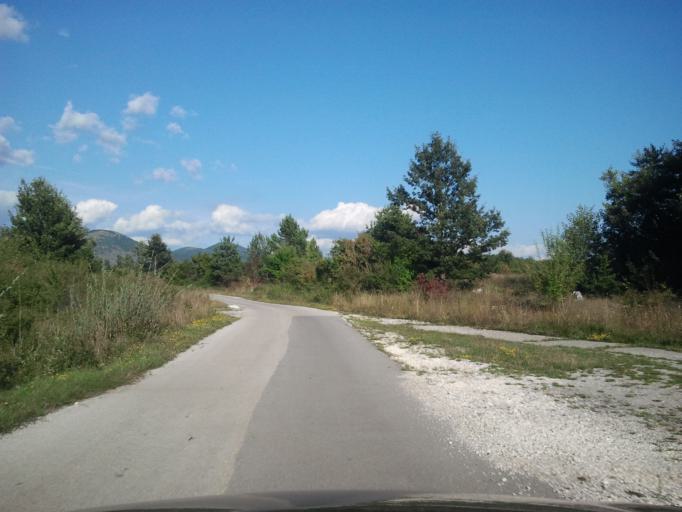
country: HR
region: Zadarska
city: Obrovac
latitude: 44.3526
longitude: 15.6772
